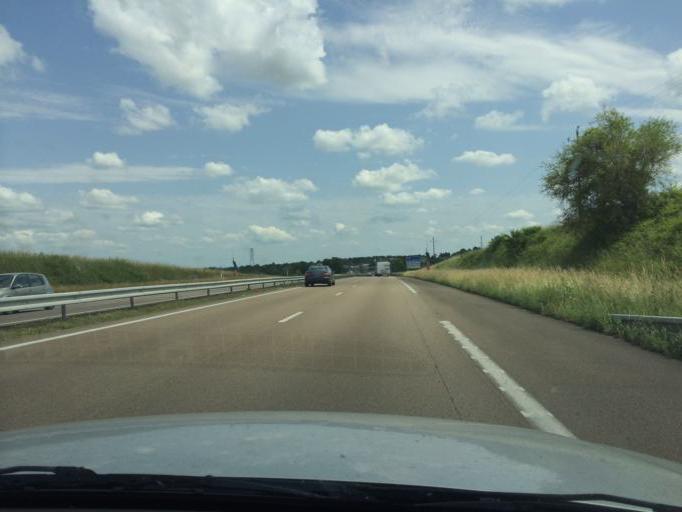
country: FR
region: Champagne-Ardenne
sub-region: Departement de la Marne
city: Verzy
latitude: 49.1277
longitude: 4.2302
